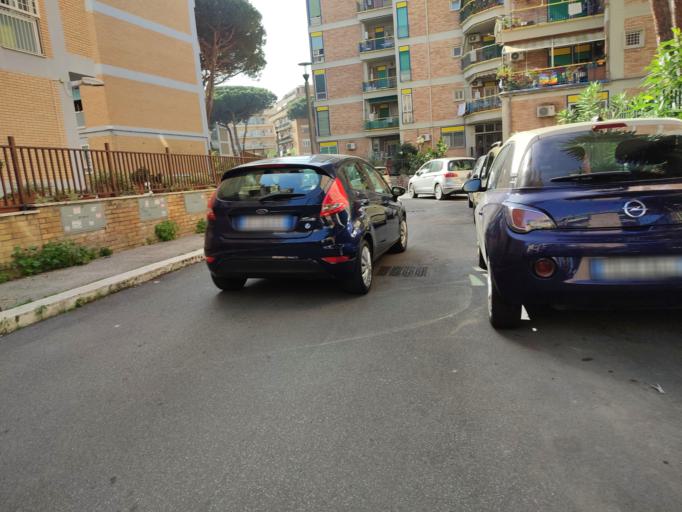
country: IT
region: Latium
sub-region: Citta metropolitana di Roma Capitale
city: Lido di Ostia
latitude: 41.7306
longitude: 12.2923
